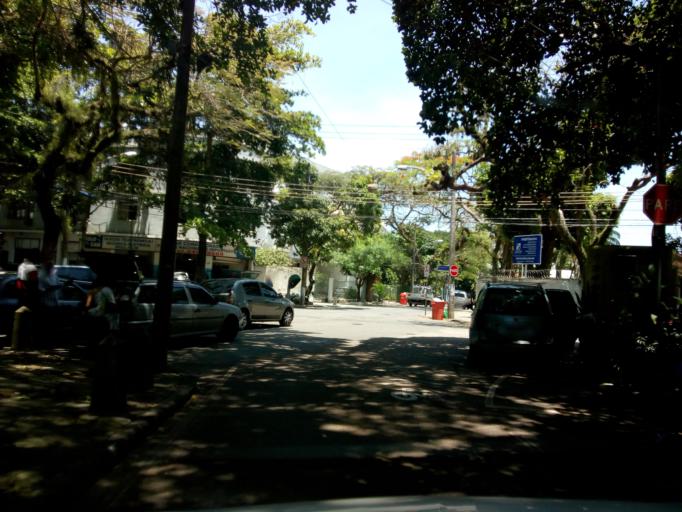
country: BR
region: Rio de Janeiro
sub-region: Rio De Janeiro
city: Rio de Janeiro
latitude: -23.0079
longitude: -43.2969
